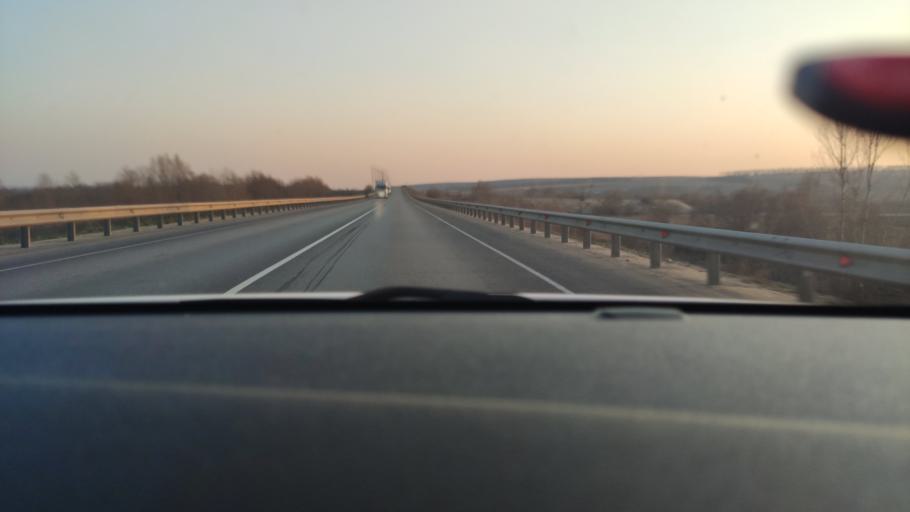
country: RU
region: Voronezj
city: Kolodeznyy
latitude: 51.3420
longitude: 39.1704
